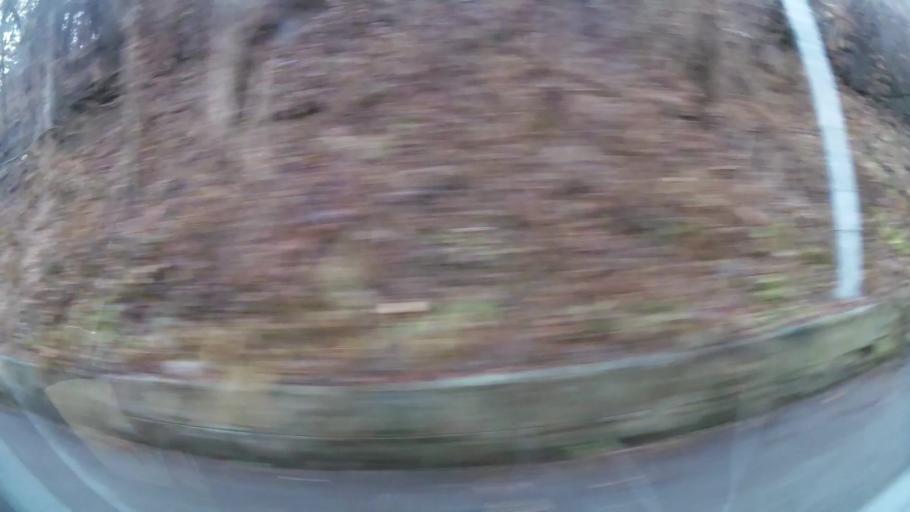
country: BG
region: Sofia-Capital
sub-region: Stolichna Obshtina
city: Sofia
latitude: 42.5885
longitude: 23.4256
